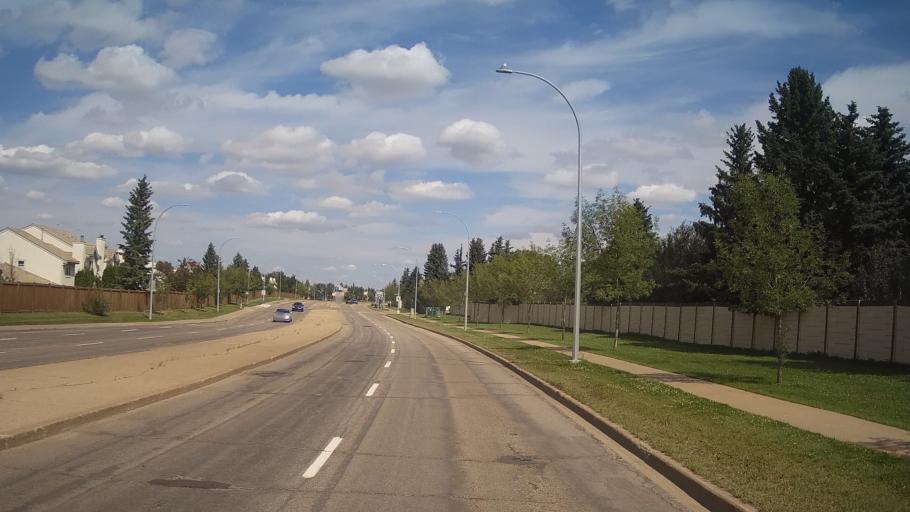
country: CA
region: Alberta
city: St. Albert
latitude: 53.5295
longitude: -113.6255
